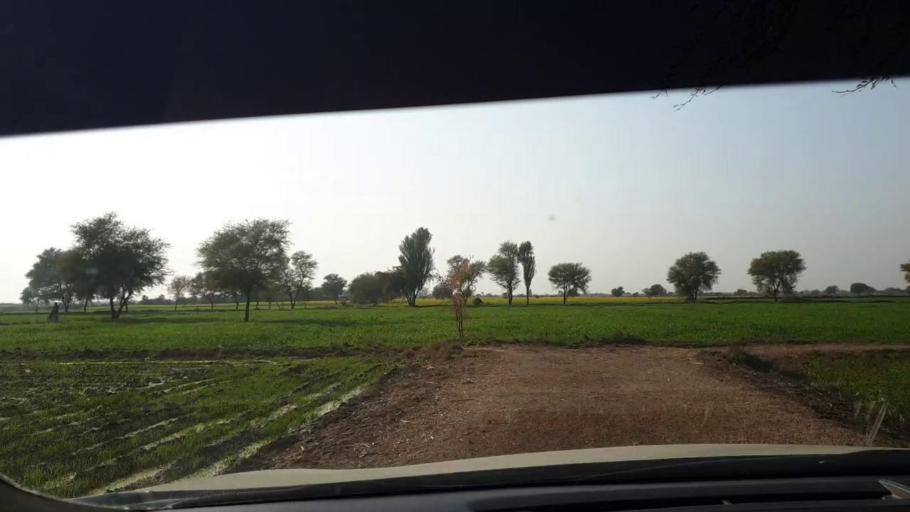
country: PK
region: Sindh
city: Berani
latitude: 25.8299
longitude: 68.7685
